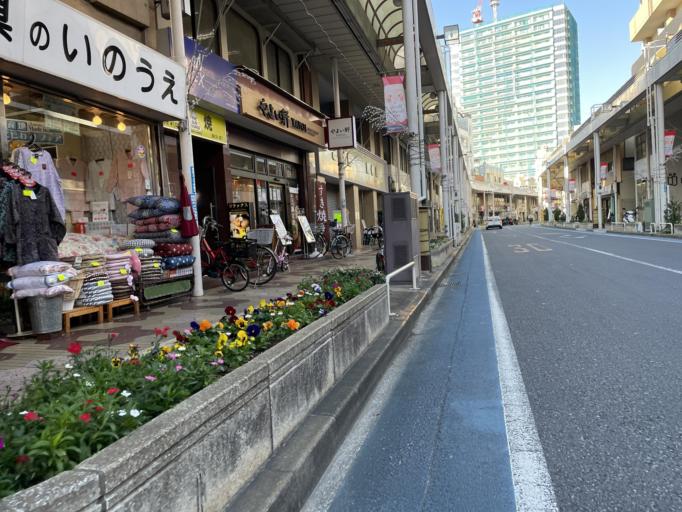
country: JP
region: Chiba
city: Matsudo
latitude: 35.7300
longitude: 139.8815
